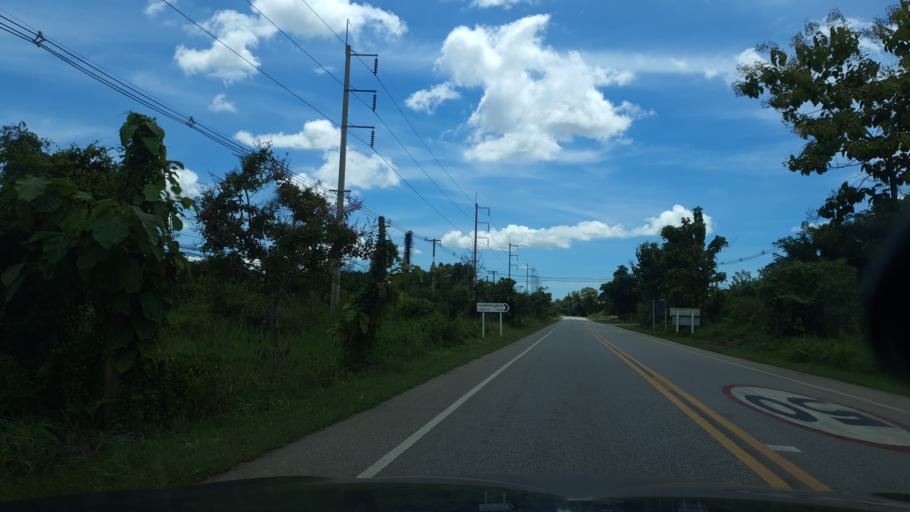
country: TH
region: Sukhothai
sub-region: Amphoe Si Satchanalai
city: Si Satchanalai
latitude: 17.4993
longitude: 99.7584
